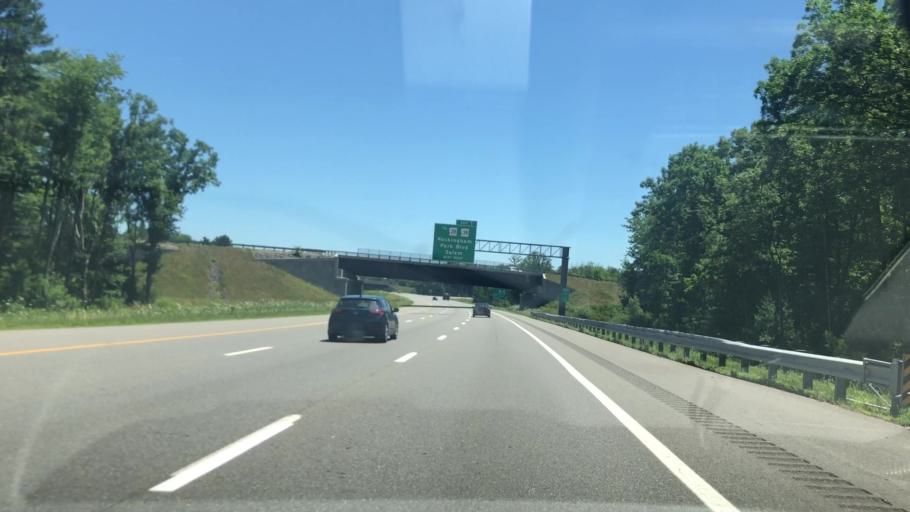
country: US
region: New Hampshire
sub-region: Rockingham County
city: Salem
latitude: 42.7621
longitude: -71.2353
